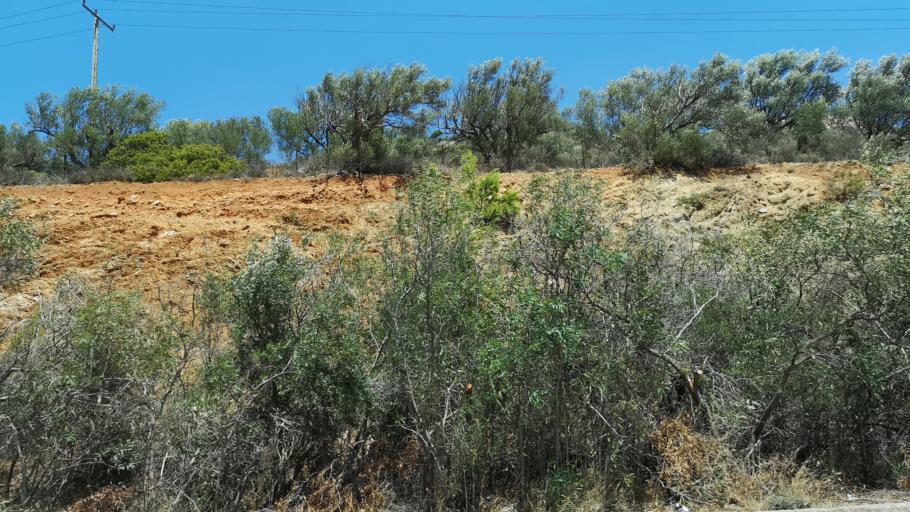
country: GR
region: Crete
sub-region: Nomos Lasithiou
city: Neapoli
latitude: 35.2262
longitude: 25.6576
